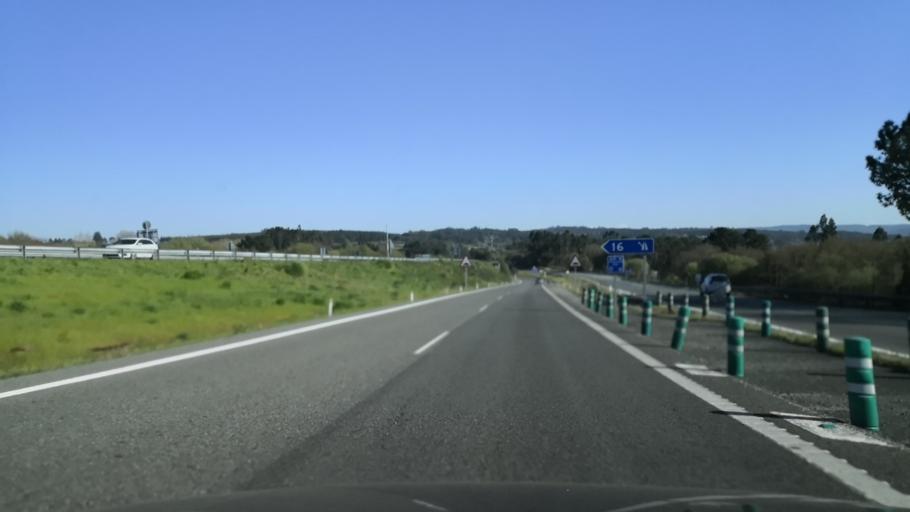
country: ES
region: Galicia
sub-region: Provincia da Coruna
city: Bergondo
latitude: 43.2792
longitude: -8.2670
